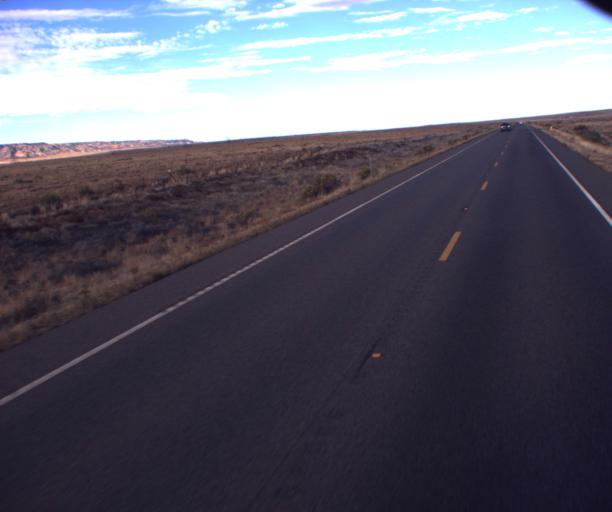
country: US
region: Arizona
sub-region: Apache County
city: Lukachukai
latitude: 36.9470
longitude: -109.2716
